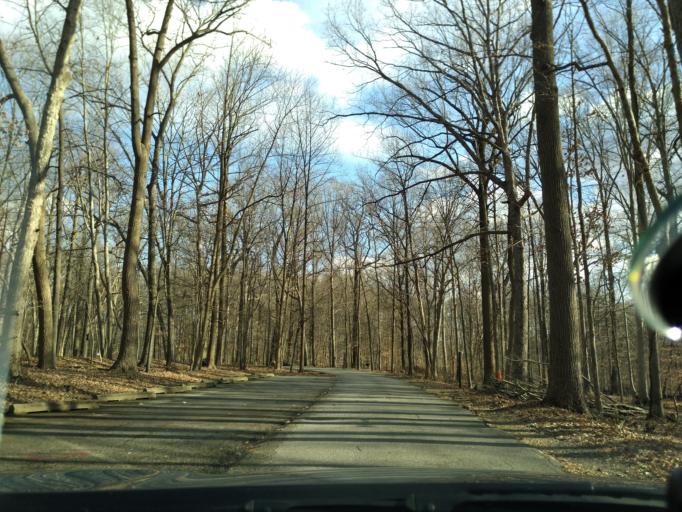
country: US
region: Maryland
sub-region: Howard County
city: Ilchester
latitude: 39.2448
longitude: -76.7464
